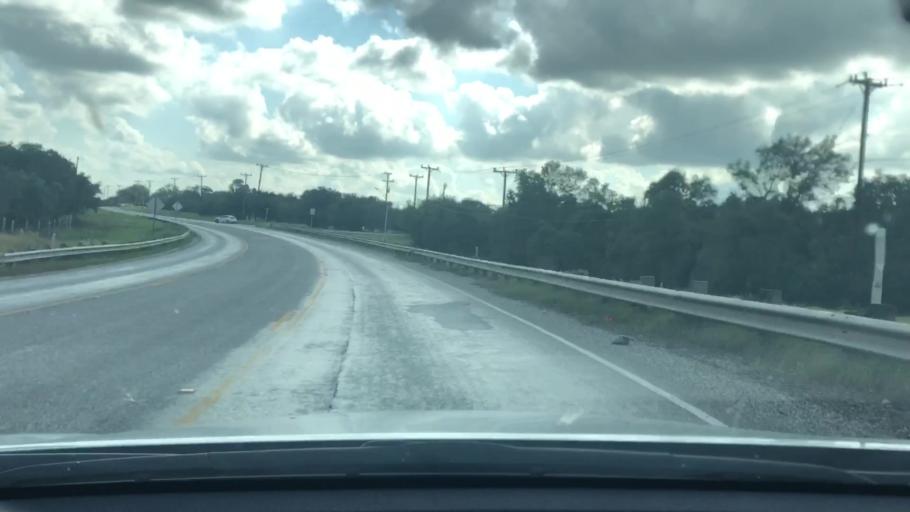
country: US
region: Texas
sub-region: Bexar County
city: Fair Oaks Ranch
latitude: 29.7537
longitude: -98.6231
